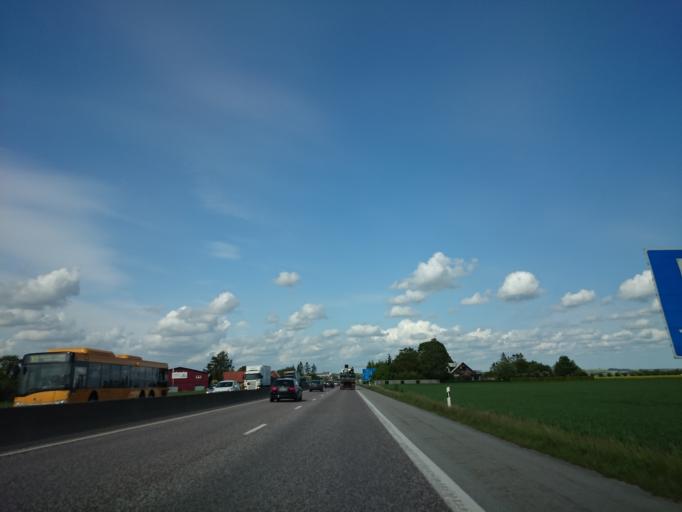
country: SE
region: Skane
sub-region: Staffanstorps Kommun
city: Hjaerup
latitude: 55.6718
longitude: 13.1706
